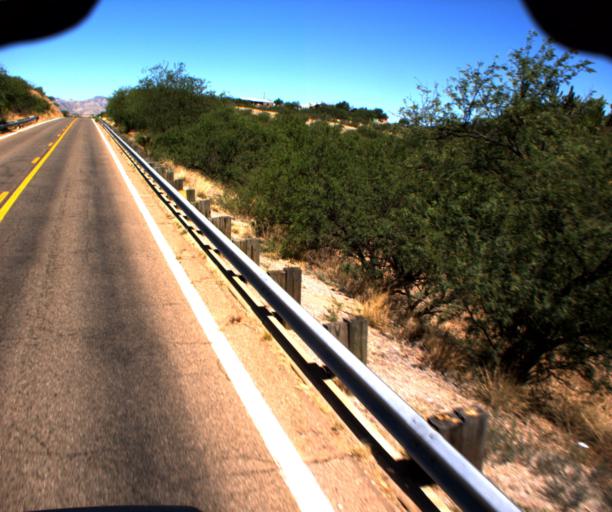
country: US
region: Arizona
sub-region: Santa Cruz County
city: Rio Rico
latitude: 31.4297
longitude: -110.9870
